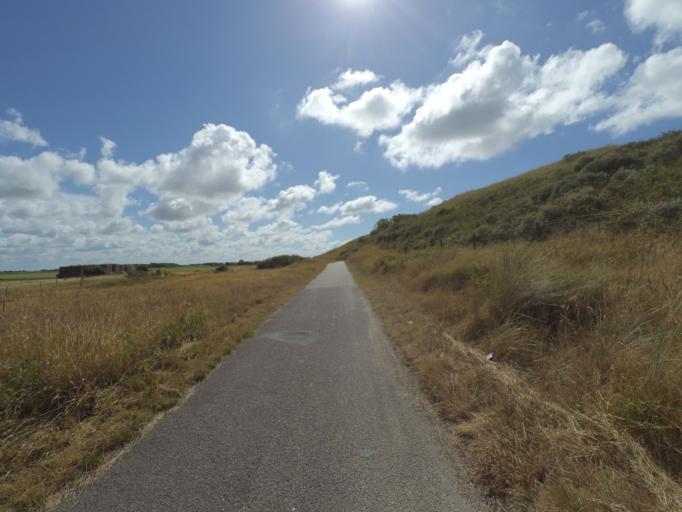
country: NL
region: North Holland
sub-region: Gemeente Texel
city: Den Burg
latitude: 53.1389
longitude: 4.8260
